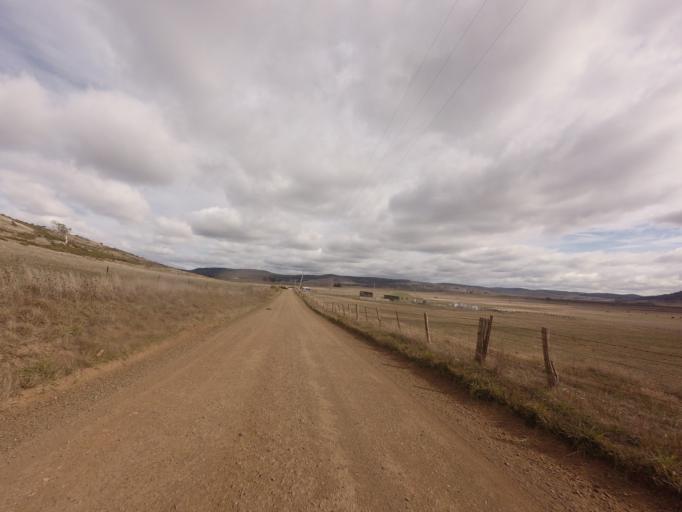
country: AU
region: Tasmania
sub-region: Brighton
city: Bridgewater
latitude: -42.4146
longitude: 147.3966
